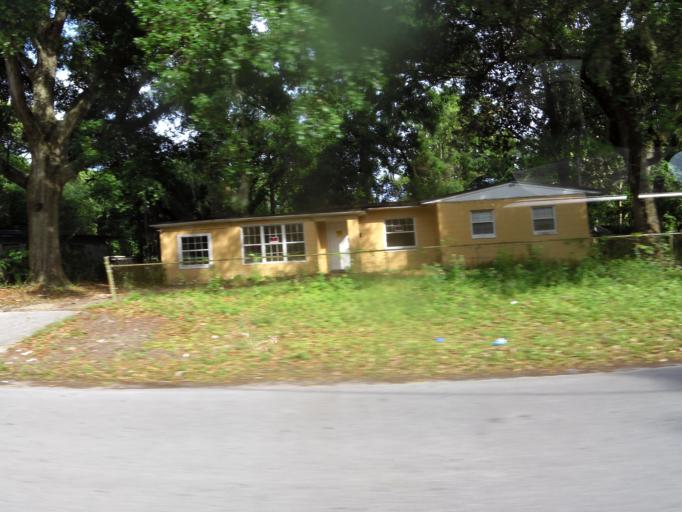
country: US
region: Florida
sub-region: Duval County
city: Jacksonville
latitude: 30.3346
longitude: -81.5877
